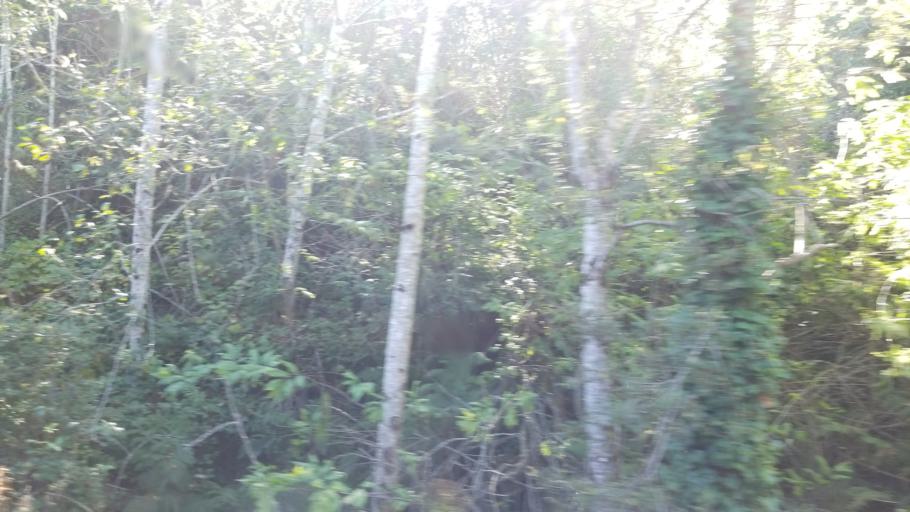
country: US
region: California
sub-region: Mendocino County
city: Fort Bragg
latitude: 39.4461
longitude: -123.7933
